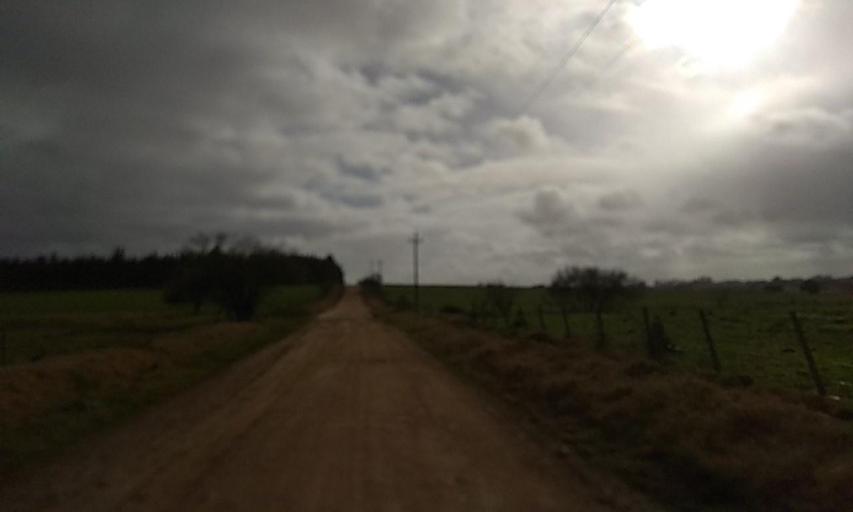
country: UY
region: Florida
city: Florida
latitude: -34.0695
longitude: -56.2319
